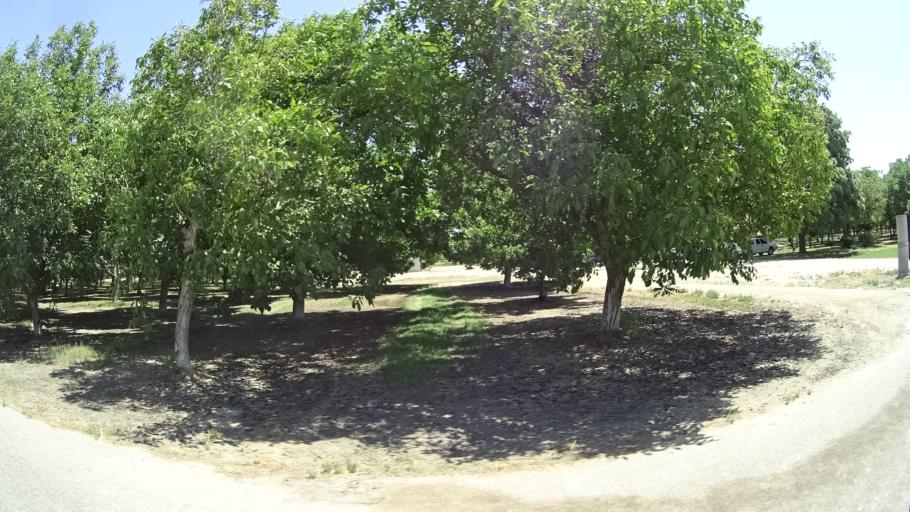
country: US
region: California
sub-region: Fresno County
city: Laton
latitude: 36.4099
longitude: -119.7269
